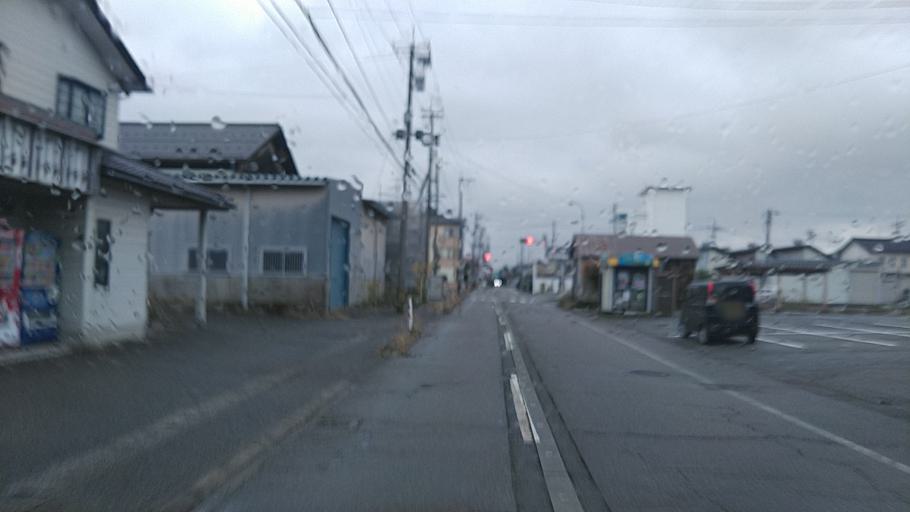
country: JP
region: Ishikawa
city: Komatsu
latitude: 36.3269
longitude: 136.3811
